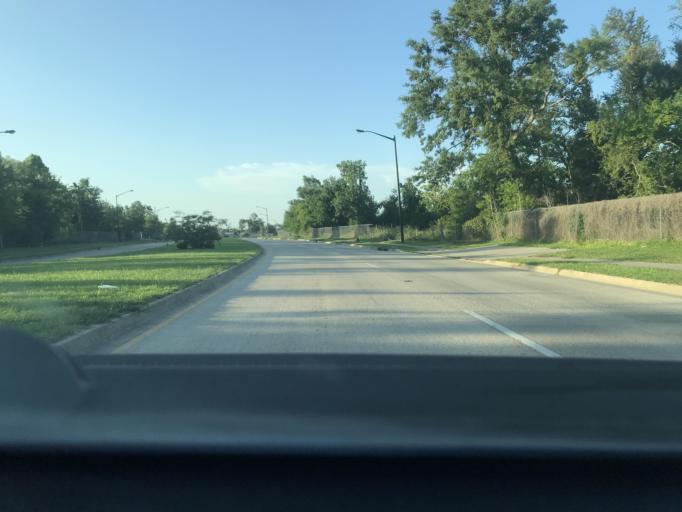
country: US
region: Louisiana
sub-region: Calcasieu Parish
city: Lake Charles
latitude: 30.2468
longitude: -93.2027
